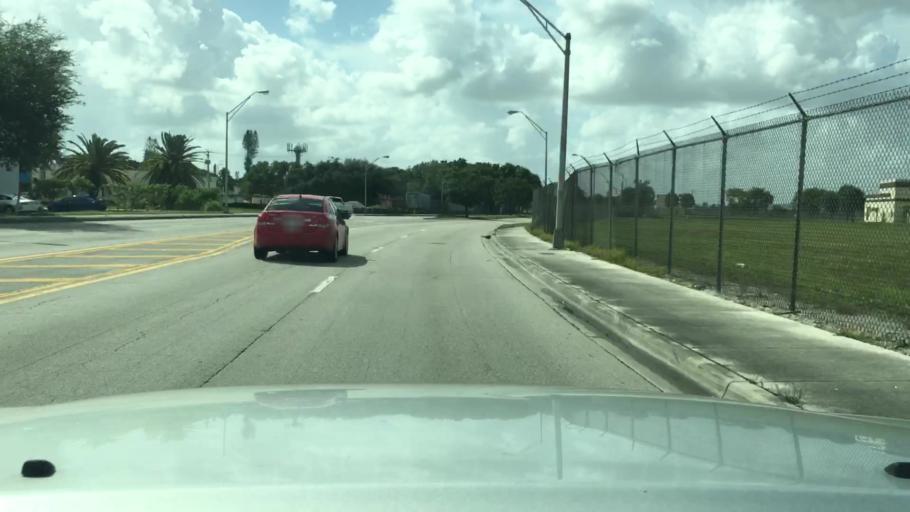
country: US
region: Florida
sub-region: Miami-Dade County
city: Opa-locka
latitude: 25.9137
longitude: -80.2585
